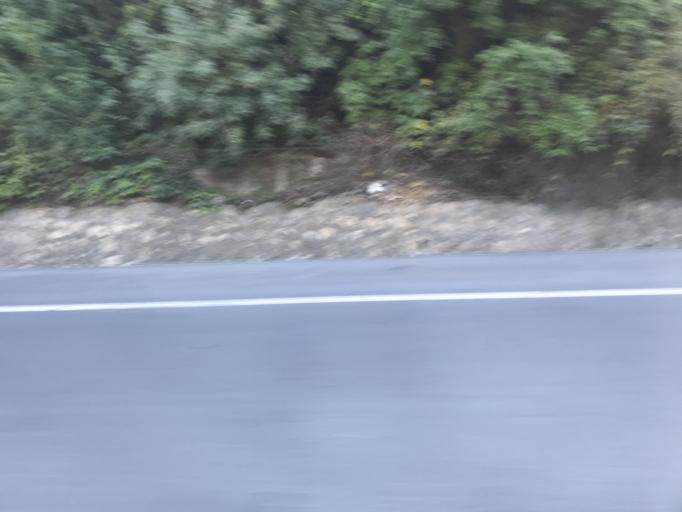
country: TR
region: Kocaeli
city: Darica
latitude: 40.7803
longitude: 29.4165
